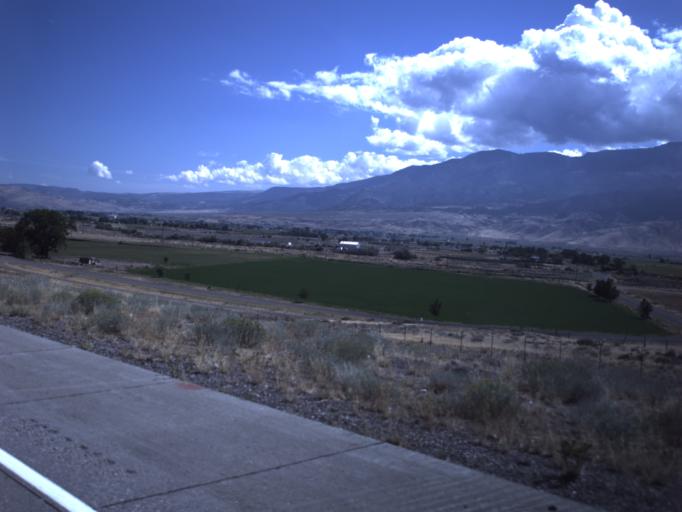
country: US
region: Utah
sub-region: Sevier County
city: Monroe
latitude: 38.6625
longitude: -112.1764
